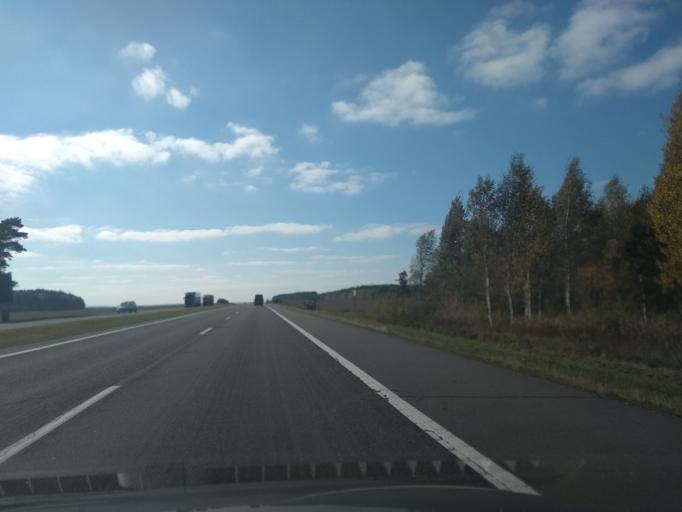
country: BY
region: Minsk
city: Haradzyeya
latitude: 53.3771
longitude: 26.5023
